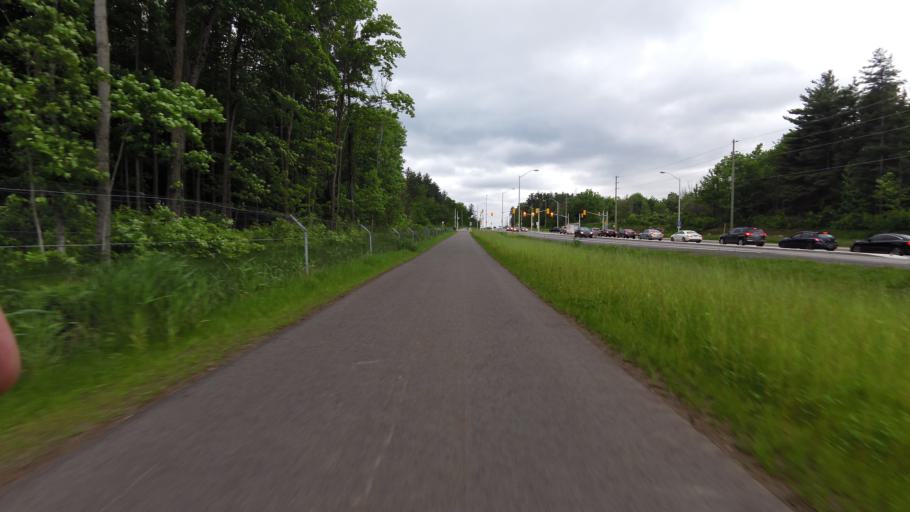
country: CA
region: Ontario
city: Bells Corners
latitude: 45.3409
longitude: -75.9372
